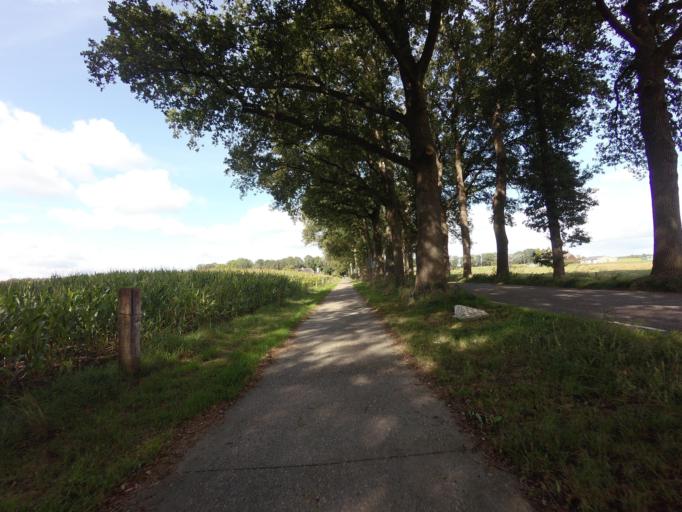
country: NL
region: Overijssel
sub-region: Gemeente Olst-Wijhe
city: Boskamp
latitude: 52.3170
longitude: 6.1661
